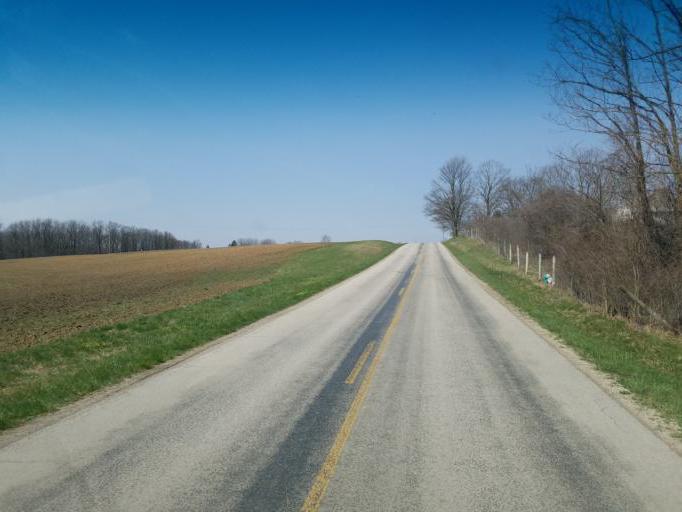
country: US
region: Ohio
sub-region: Wyandot County
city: Upper Sandusky
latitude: 40.8765
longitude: -83.2423
